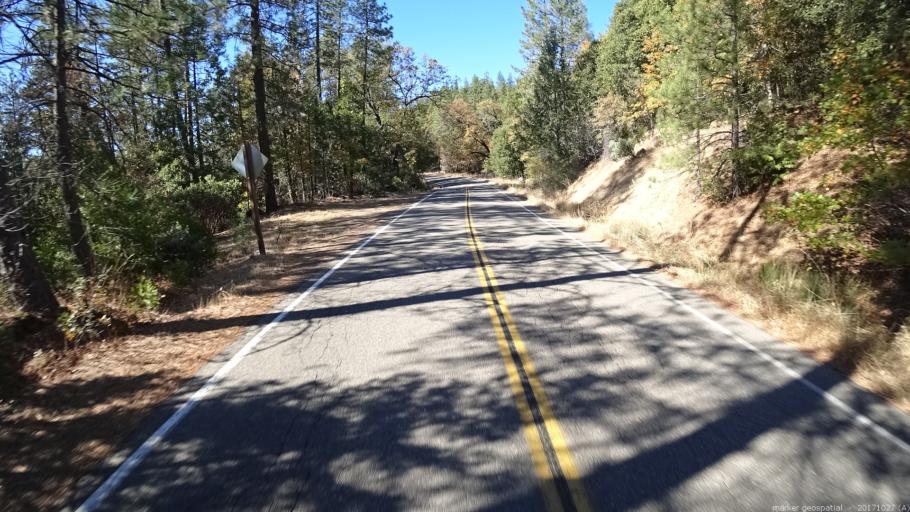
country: US
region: California
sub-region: Shasta County
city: Shingletown
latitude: 40.7054
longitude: -121.9268
